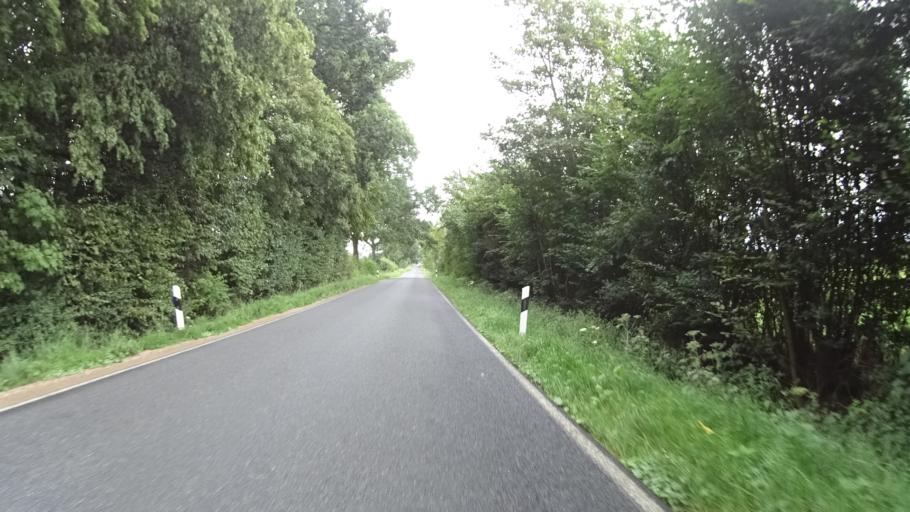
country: DE
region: Schleswig-Holstein
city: Kuhsen
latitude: 53.6842
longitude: 10.6030
